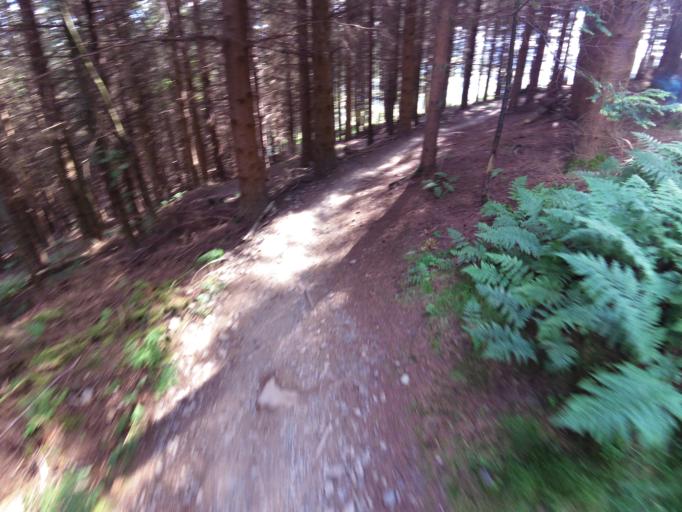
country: GB
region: Scotland
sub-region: The Scottish Borders
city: Peebles
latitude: 55.6509
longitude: -3.1365
